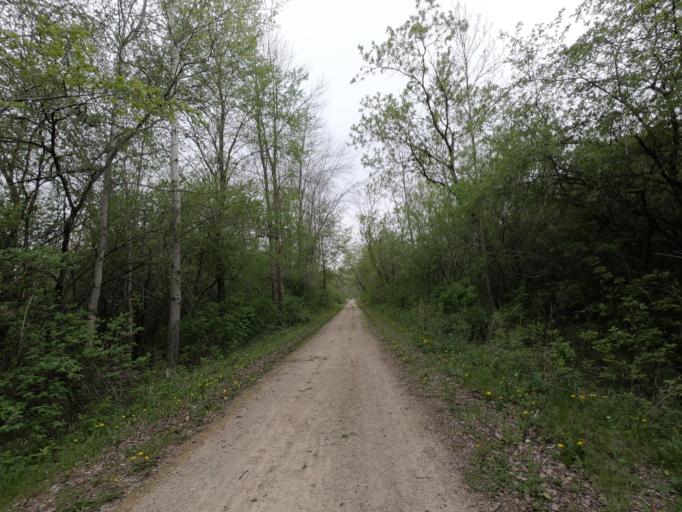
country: US
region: Wisconsin
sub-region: Jefferson County
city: Johnson Creek
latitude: 43.0296
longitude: -88.7433
